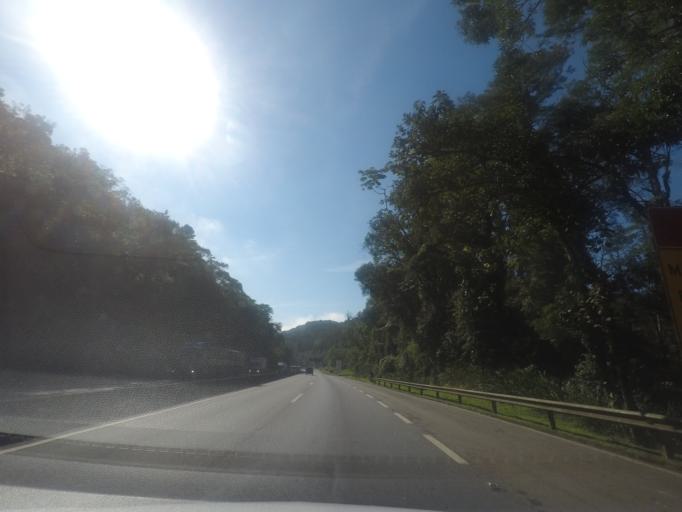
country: BR
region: Parana
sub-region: Piraquara
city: Piraquara
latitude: -25.5971
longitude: -48.9029
